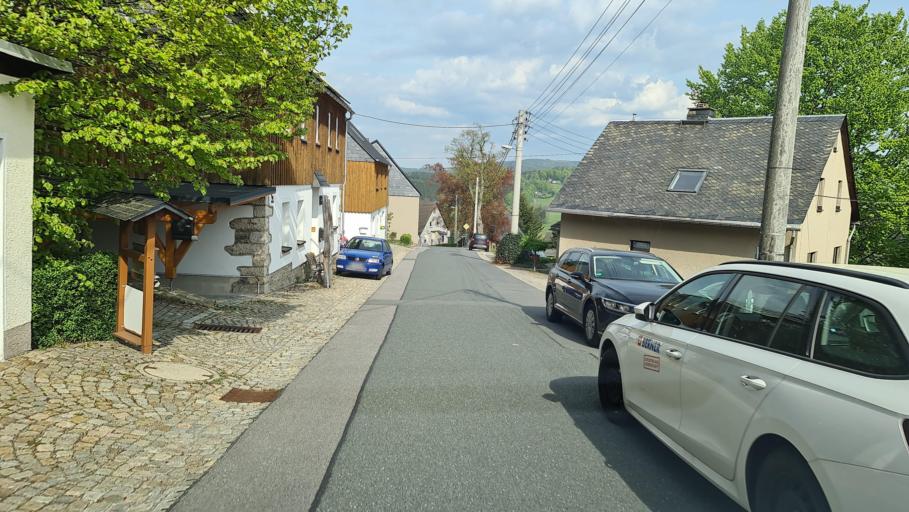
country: DE
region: Saxony
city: Schwarzenberg
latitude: 50.5186
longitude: 12.7716
